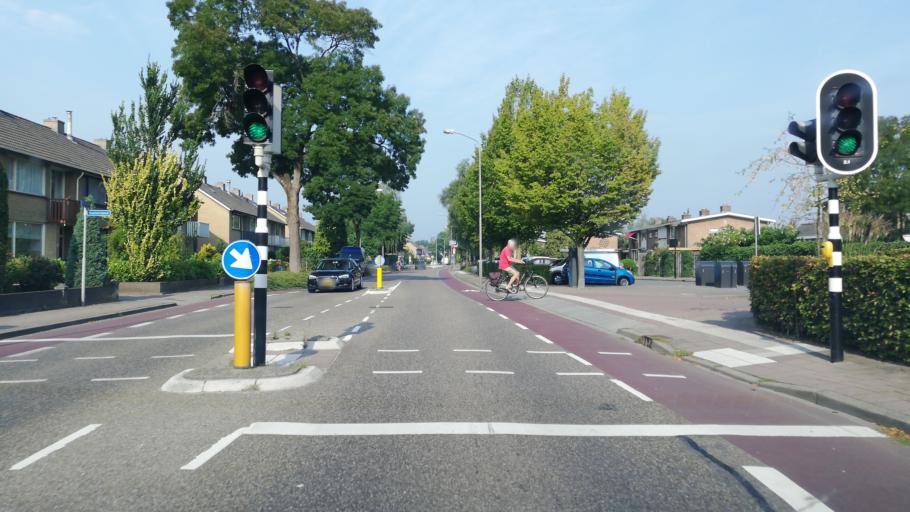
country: NL
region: Gelderland
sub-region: Gemeente Ermelo
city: Ermelo
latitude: 52.2941
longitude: 5.6250
